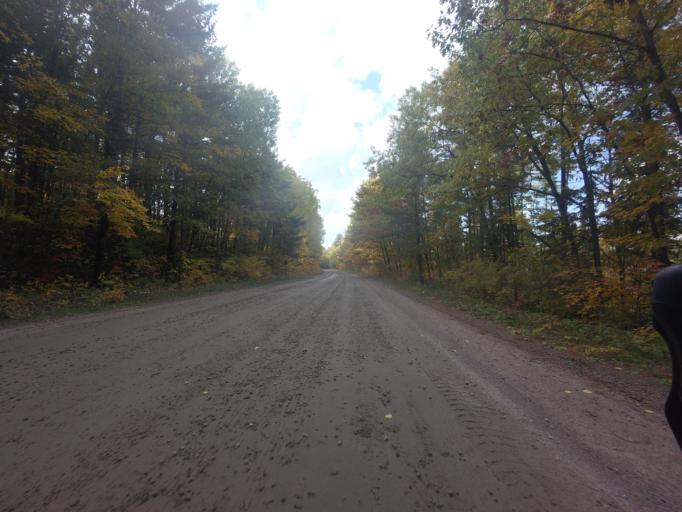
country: CA
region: Ontario
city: Deep River
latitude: 45.8532
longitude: -77.5388
